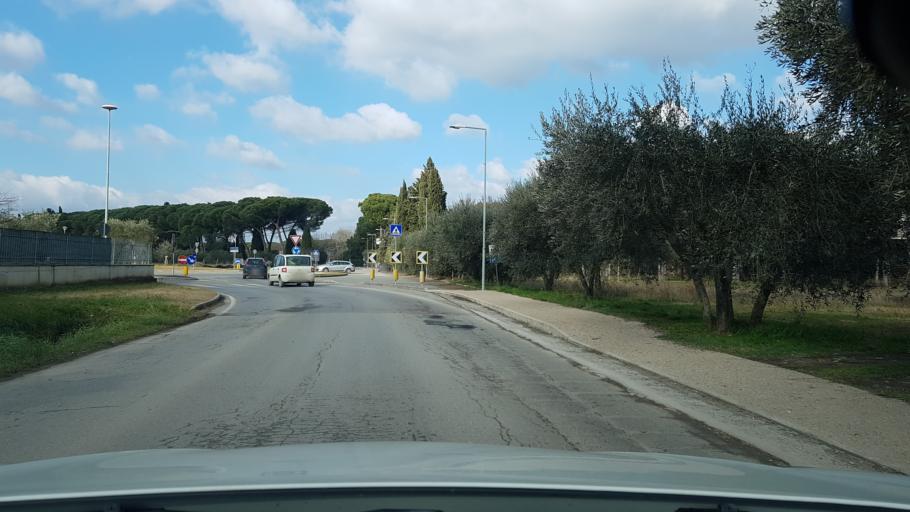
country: IT
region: Umbria
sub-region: Provincia di Perugia
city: Castiglione del Lago
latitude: 43.1297
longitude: 12.0438
